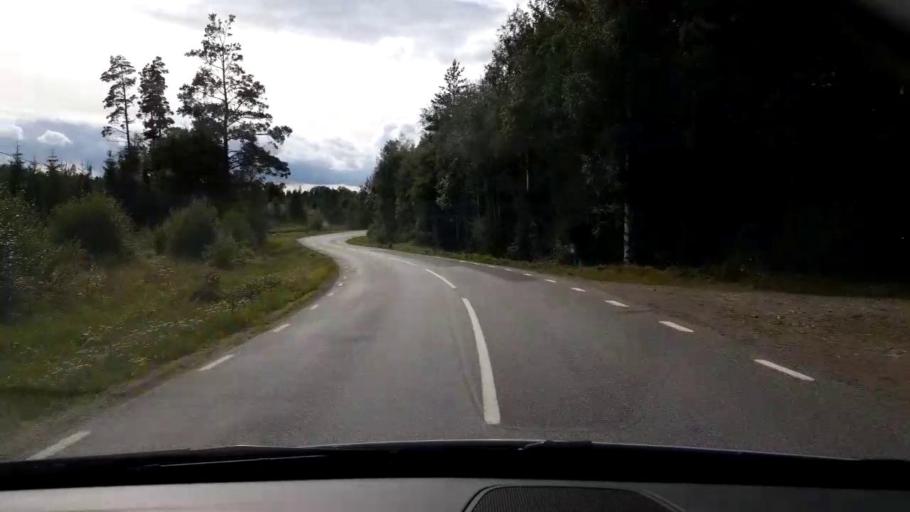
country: SE
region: Joenkoeping
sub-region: Vetlanda Kommun
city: Landsbro
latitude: 57.3804
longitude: 14.9835
